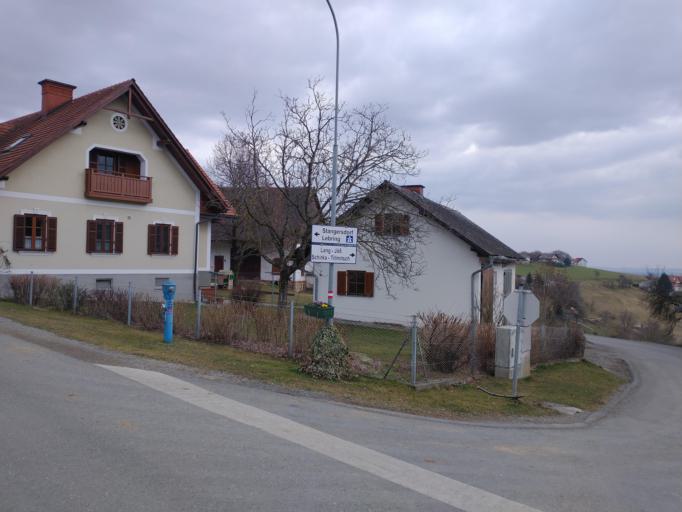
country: AT
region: Styria
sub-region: Politischer Bezirk Leibnitz
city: Lang
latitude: 46.8481
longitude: 15.4828
